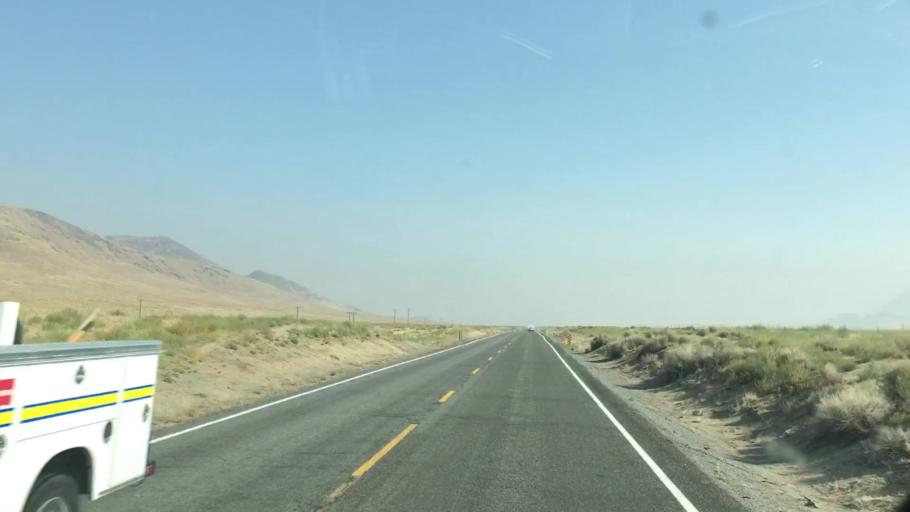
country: US
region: Nevada
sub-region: Lyon County
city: Fernley
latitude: 40.3938
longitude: -119.3336
